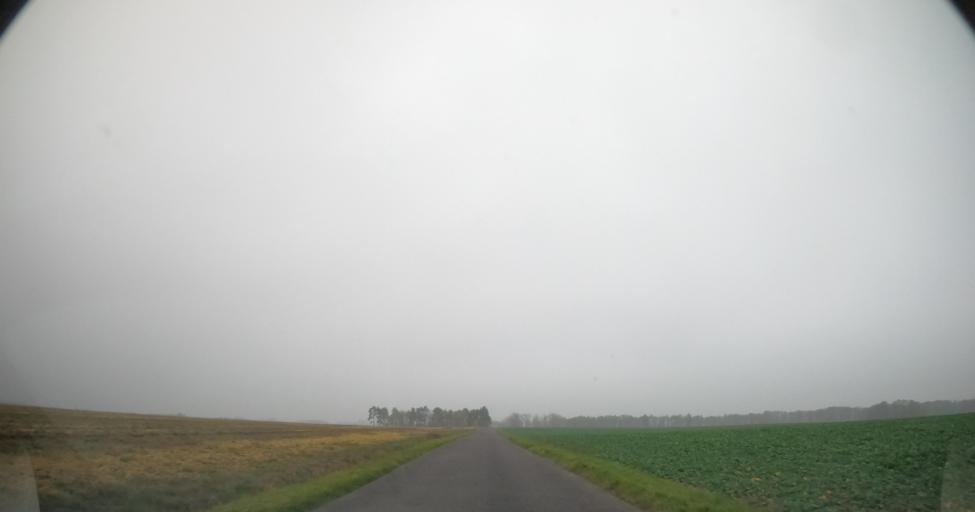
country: PL
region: West Pomeranian Voivodeship
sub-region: Powiat drawski
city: Drawsko Pomorskie
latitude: 53.6071
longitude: 15.7405
